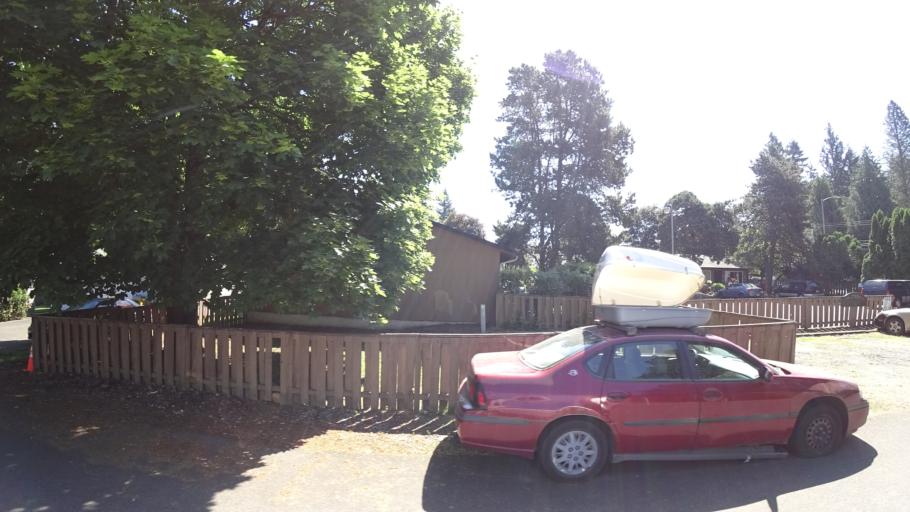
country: US
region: Oregon
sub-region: Multnomah County
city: Lents
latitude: 45.4770
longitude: -122.5399
